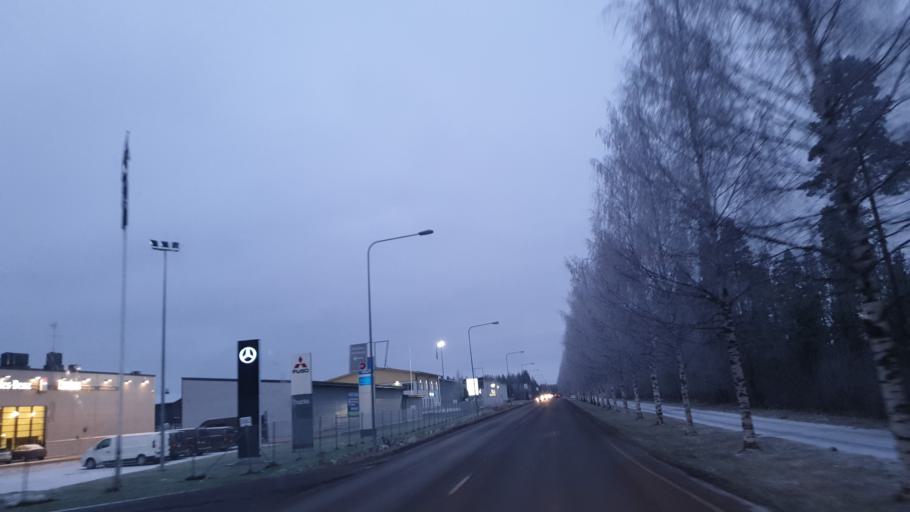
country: FI
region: Southern Ostrobothnia
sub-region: Seinaejoki
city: Nurmo
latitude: 62.7845
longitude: 22.9010
